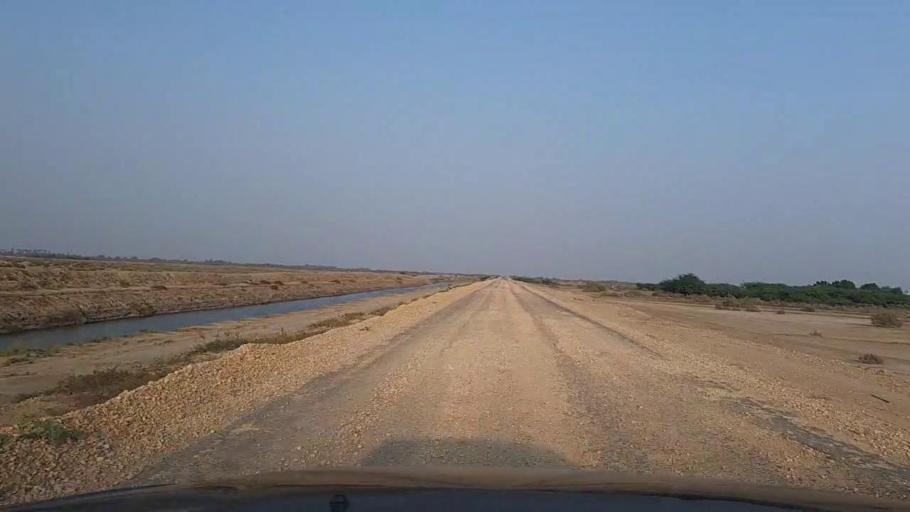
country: PK
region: Sindh
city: Mirpur Sakro
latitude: 24.4384
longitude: 67.7732
